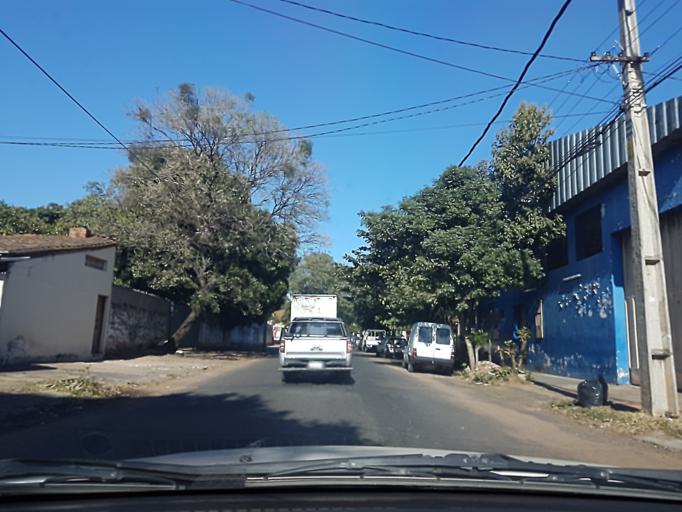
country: PY
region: Central
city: Lambare
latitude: -25.3155
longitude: -57.5876
